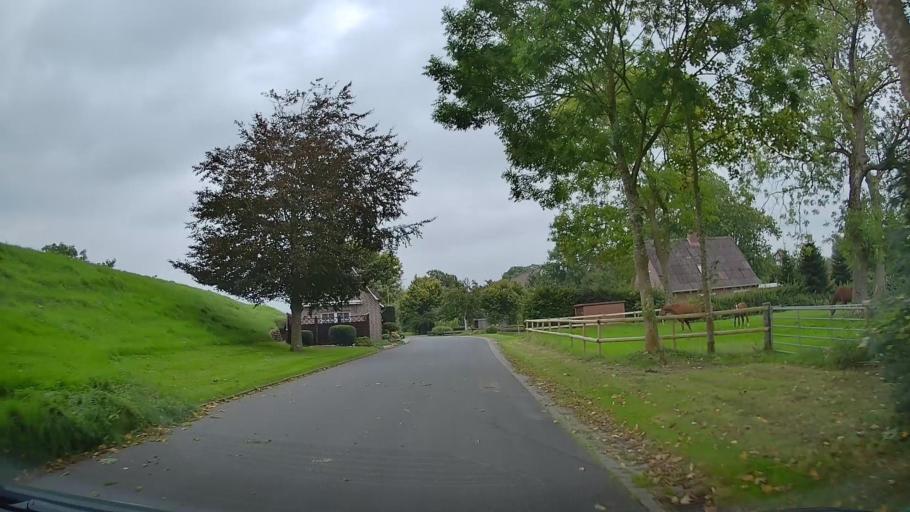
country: DE
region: Lower Saxony
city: Balje
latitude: 53.8309
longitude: 9.1398
